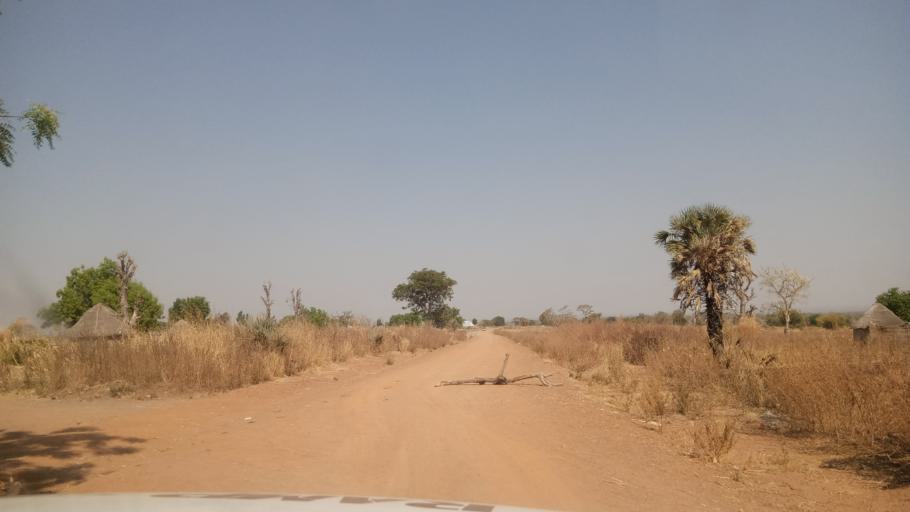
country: NG
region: Adamawa
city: Mayo Belwa
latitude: 9.1574
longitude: 12.1273
